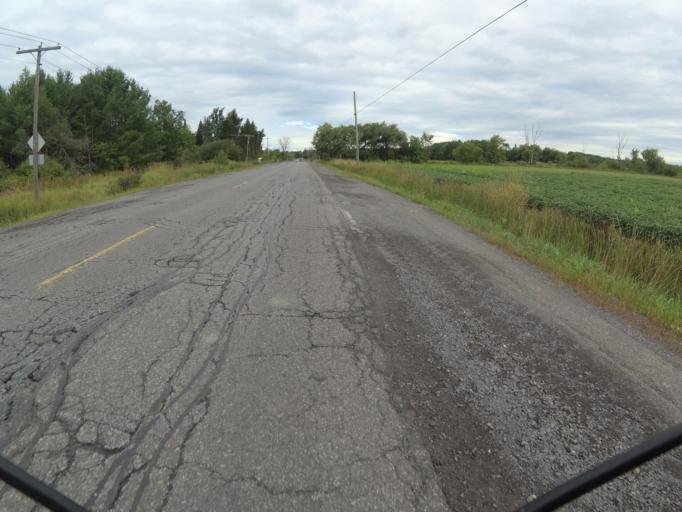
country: CA
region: Ontario
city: Bourget
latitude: 45.3848
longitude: -75.2754
